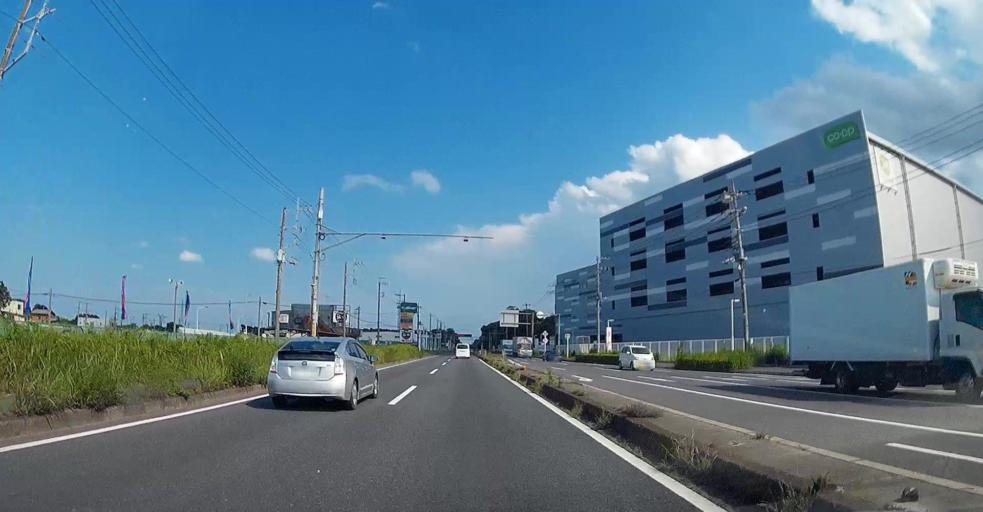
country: JP
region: Chiba
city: Noda
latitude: 35.9908
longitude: 139.8514
